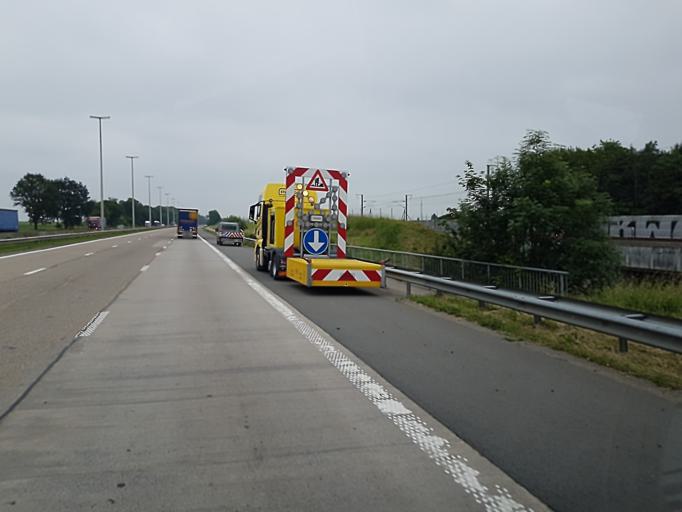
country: BE
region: Wallonia
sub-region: Province de Liege
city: Oreye
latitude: 50.7016
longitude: 5.3437
